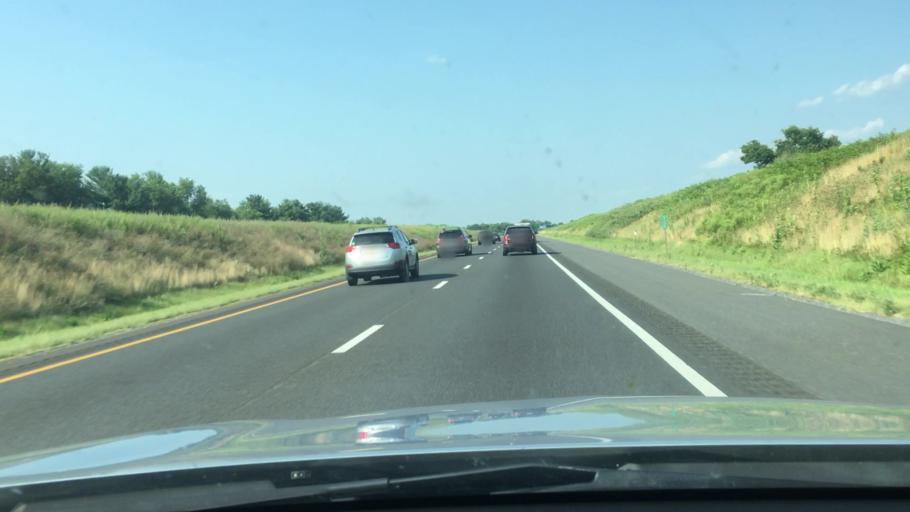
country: US
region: Virginia
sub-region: Shenandoah County
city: Mount Jackson
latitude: 38.7281
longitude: -78.6553
